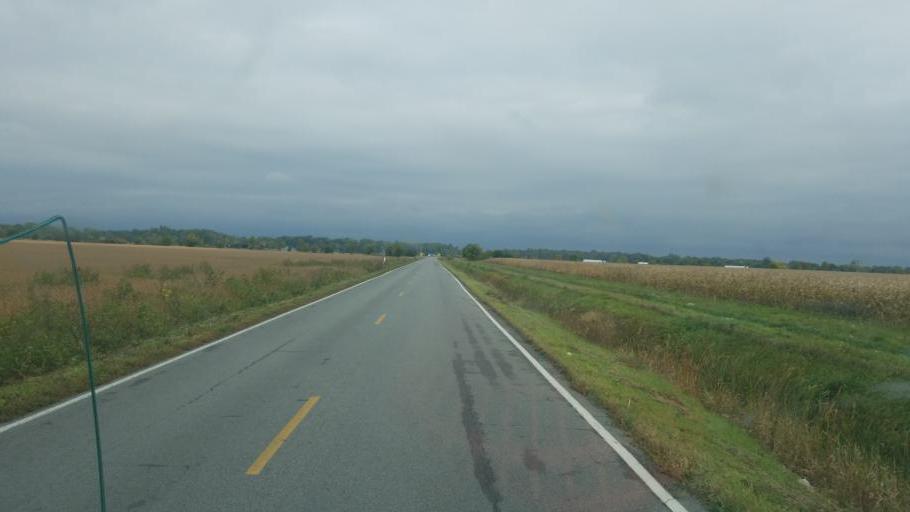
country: US
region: Ohio
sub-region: Wood County
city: Bowling Green
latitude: 41.3439
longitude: -83.6698
